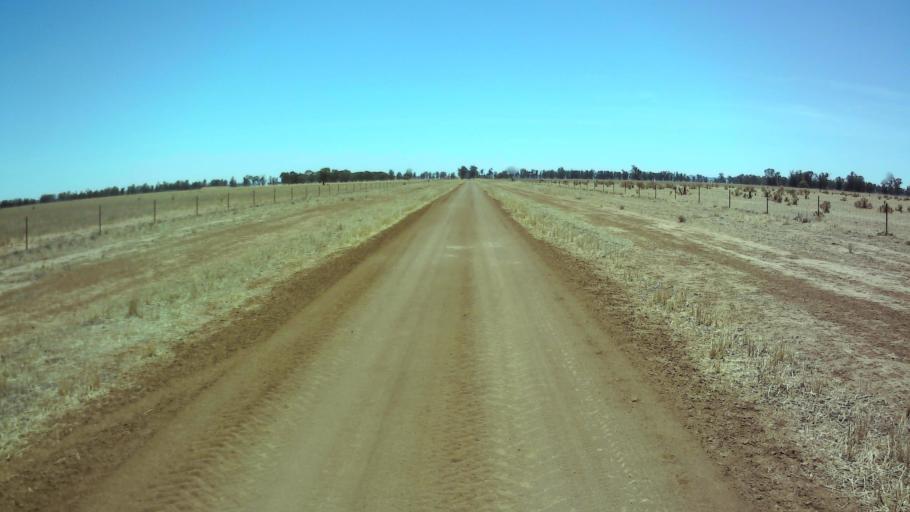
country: AU
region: New South Wales
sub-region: Weddin
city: Grenfell
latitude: -33.9834
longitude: 147.7356
